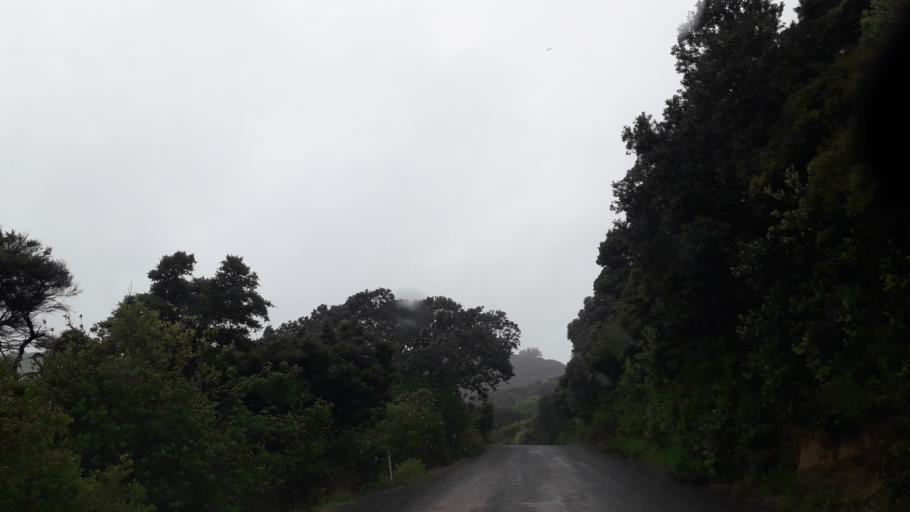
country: NZ
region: Northland
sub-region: Far North District
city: Paihia
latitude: -35.2277
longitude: 174.2635
